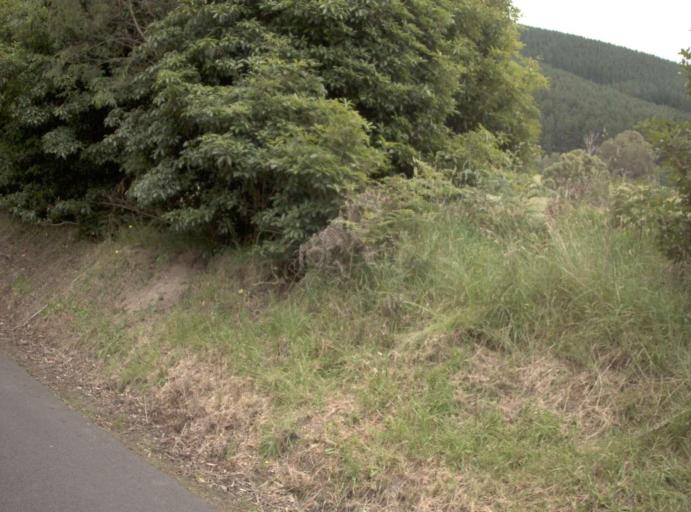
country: AU
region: Victoria
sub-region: Latrobe
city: Traralgon
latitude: -38.4864
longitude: 146.6081
